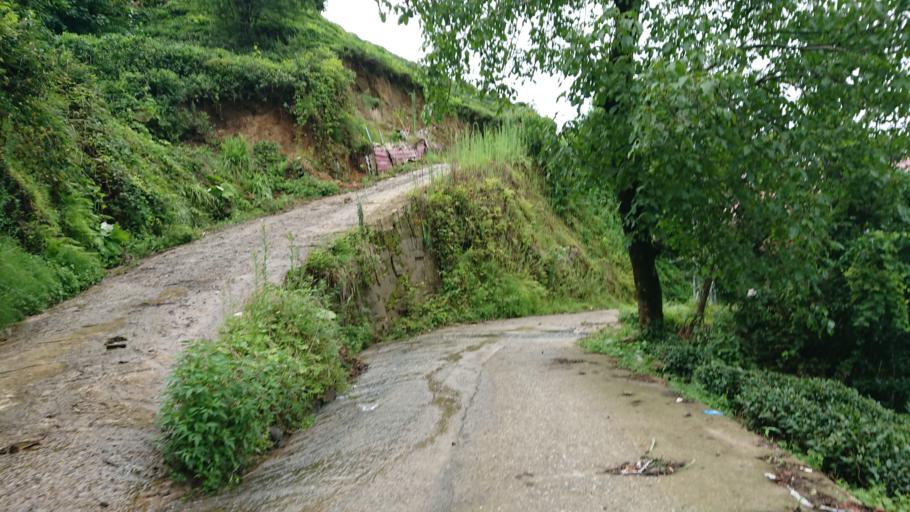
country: TR
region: Rize
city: Rize
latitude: 40.9750
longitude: 40.4854
